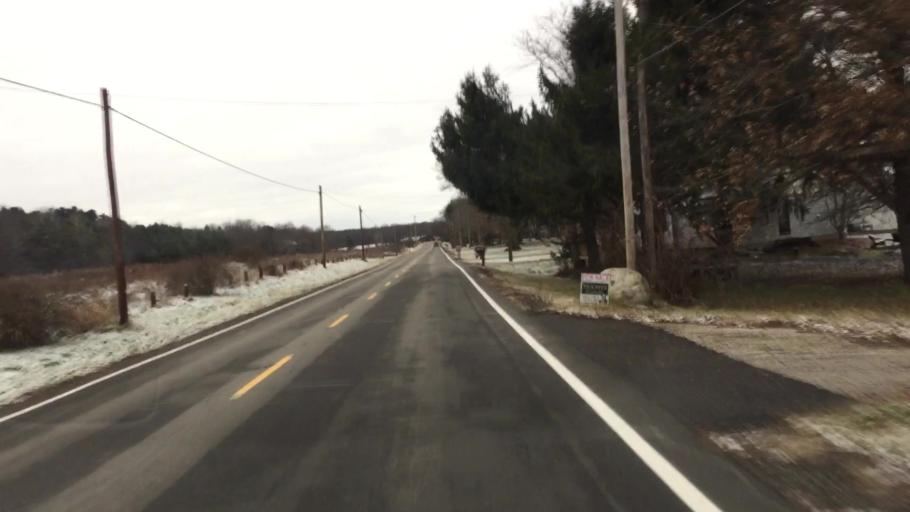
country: US
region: Ohio
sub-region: Summit County
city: Norton
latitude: 41.0718
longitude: -81.6312
